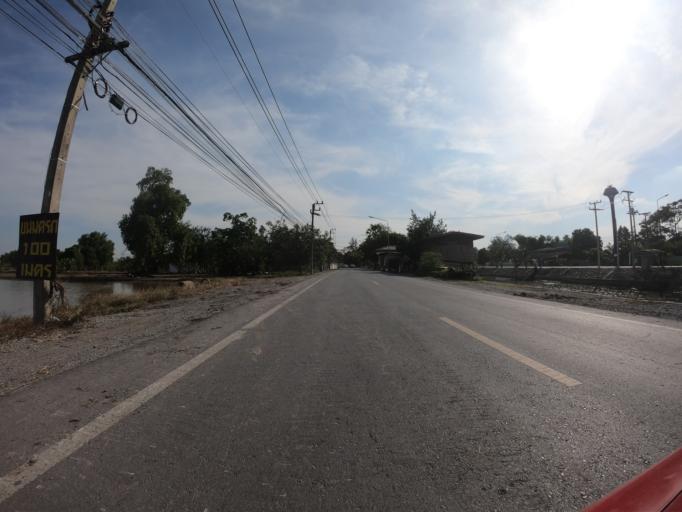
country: TH
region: Pathum Thani
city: Thanyaburi
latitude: 13.9963
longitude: 100.7304
